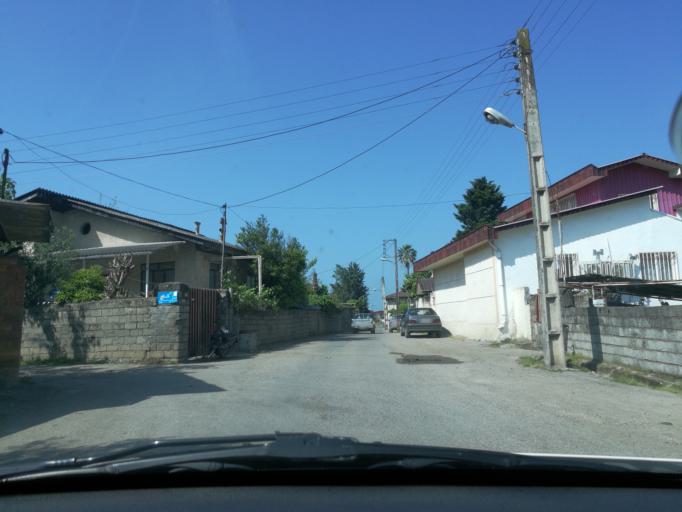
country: IR
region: Mazandaran
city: Chalus
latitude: 36.6672
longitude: 51.4312
